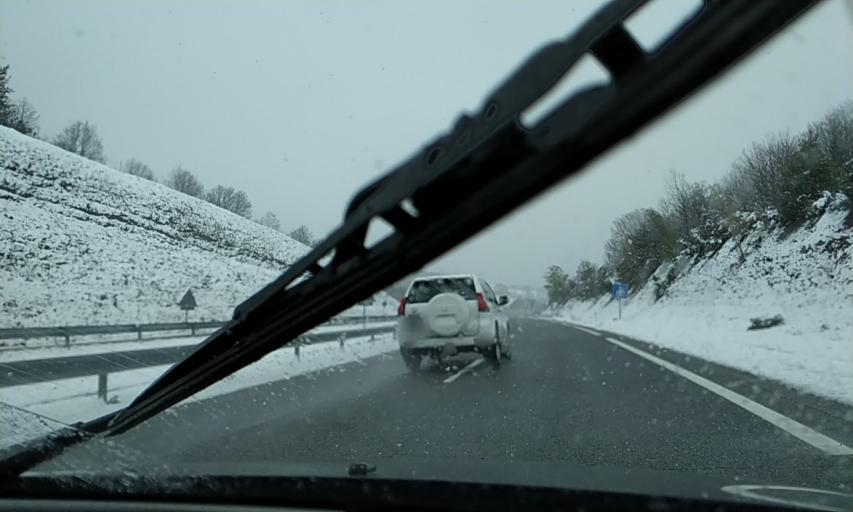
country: ES
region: Galicia
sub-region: Provincia de Ourense
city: Rios
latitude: 41.9804
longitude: -7.2977
